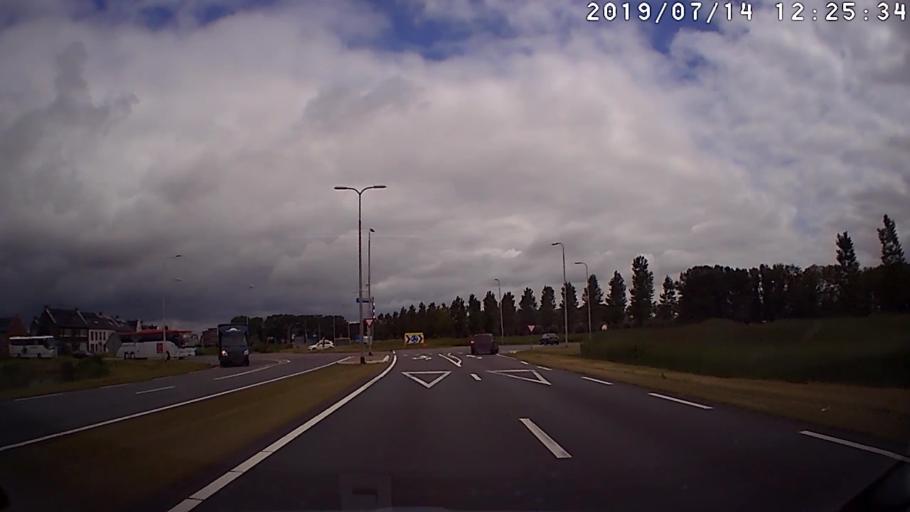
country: NL
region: Overijssel
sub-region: Gemeente Kampen
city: Kampen
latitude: 52.5323
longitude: 5.9182
